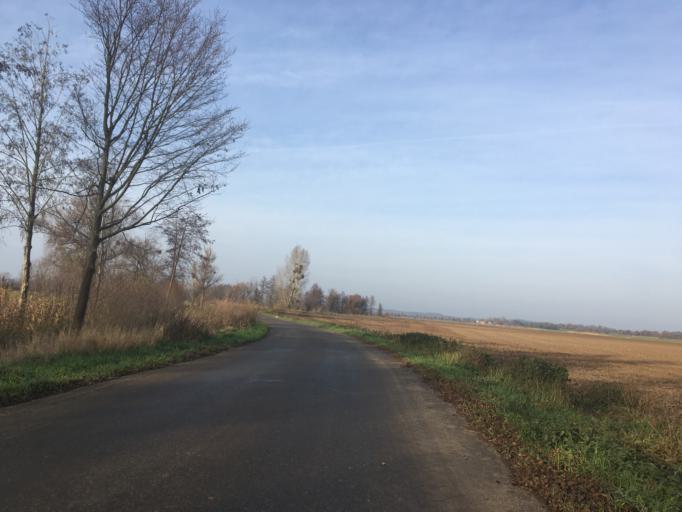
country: DE
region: Brandenburg
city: Wriezen
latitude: 52.7607
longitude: 14.1143
